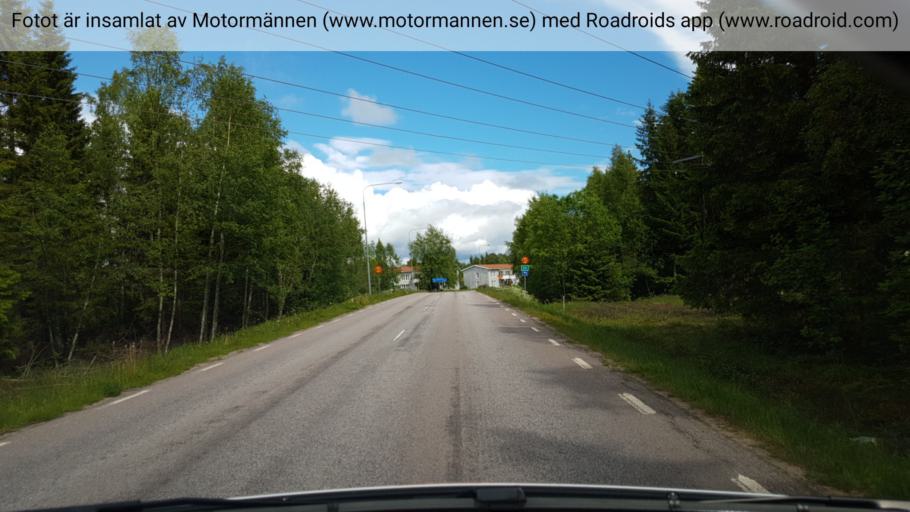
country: SE
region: Vaesterbotten
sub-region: Umea Kommun
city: Hoernefors
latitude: 63.6218
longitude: 19.8951
